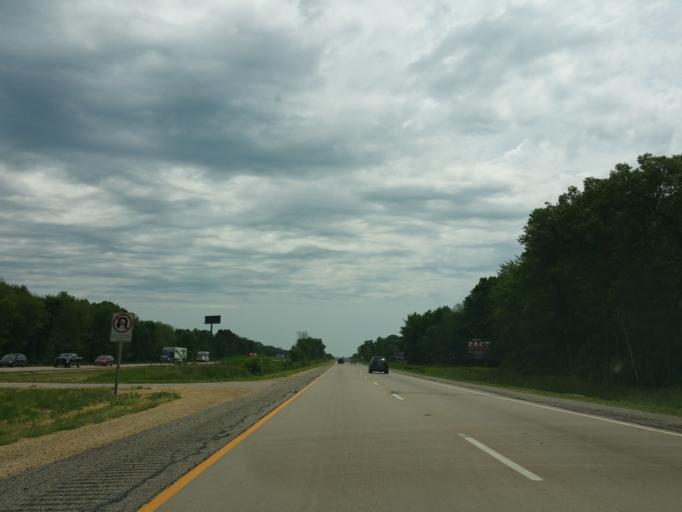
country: US
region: Wisconsin
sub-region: Columbia County
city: Wisconsin Dells
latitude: 43.7139
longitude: -89.8880
